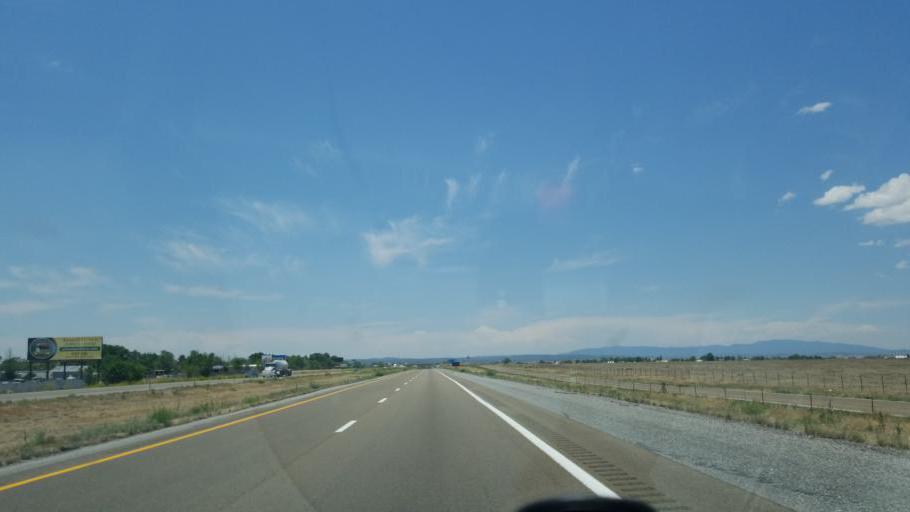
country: US
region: New Mexico
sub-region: Torrance County
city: Moriarty
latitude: 35.0071
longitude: -106.0267
